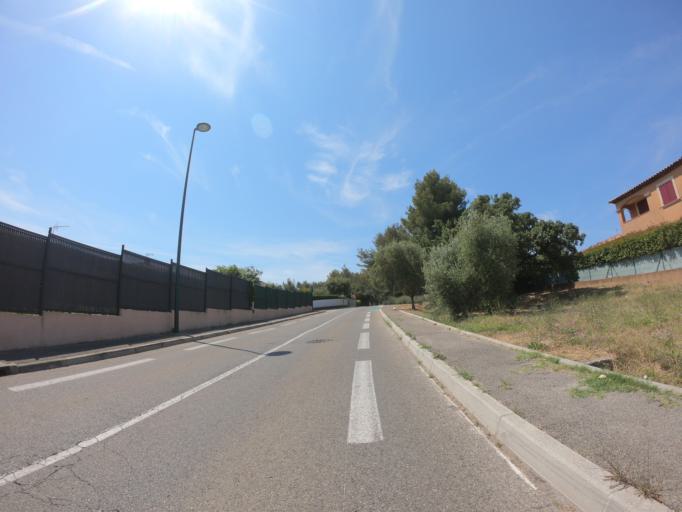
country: FR
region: Provence-Alpes-Cote d'Azur
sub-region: Departement du Var
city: La Garde
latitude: 43.1196
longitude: 5.9992
